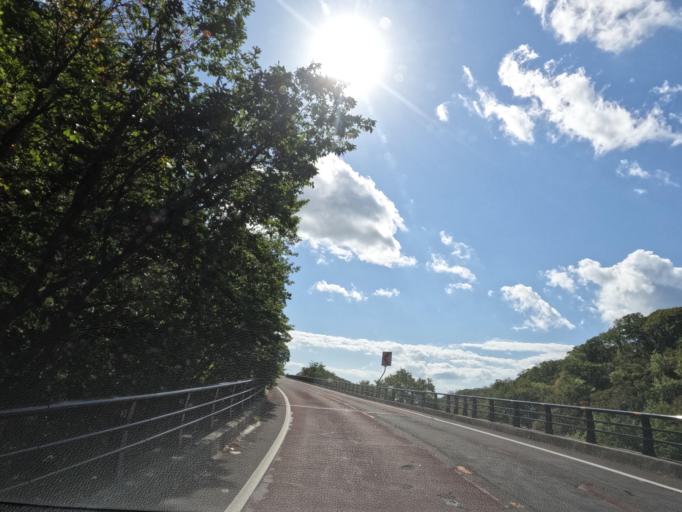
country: JP
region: Hokkaido
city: Shiraoi
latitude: 42.4806
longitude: 141.1448
